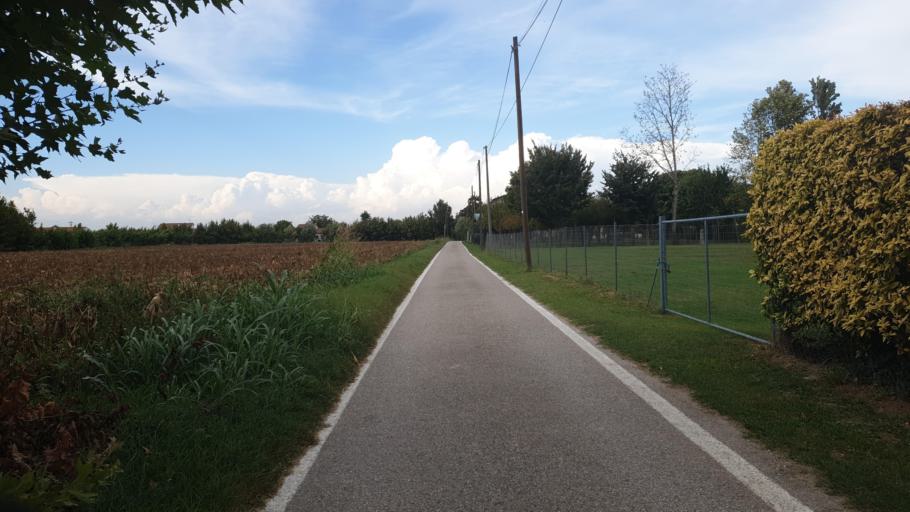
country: IT
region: Veneto
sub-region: Provincia di Padova
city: Bertipaglia
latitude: 45.3309
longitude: 11.8796
